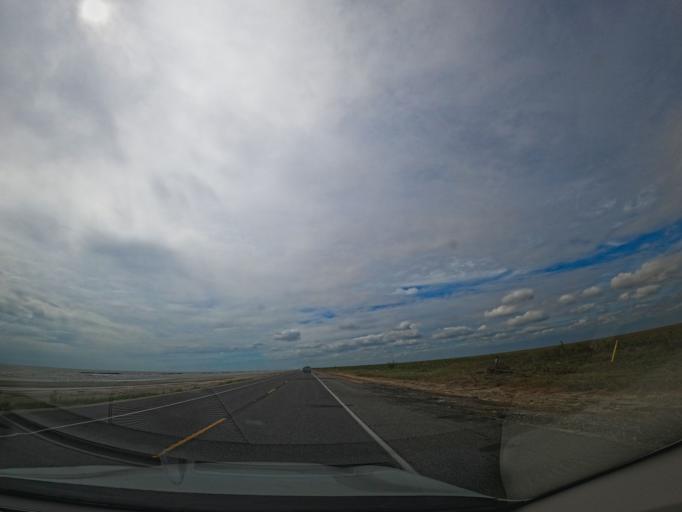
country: US
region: Louisiana
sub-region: Cameron Parish
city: Cameron
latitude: 29.7681
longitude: -93.5055
